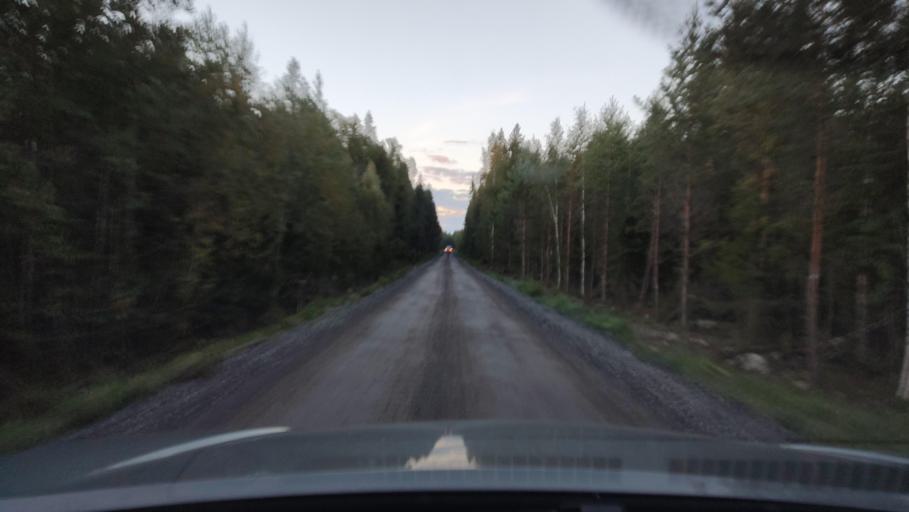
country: FI
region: Southern Ostrobothnia
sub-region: Suupohja
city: Karijoki
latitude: 62.1972
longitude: 21.5749
